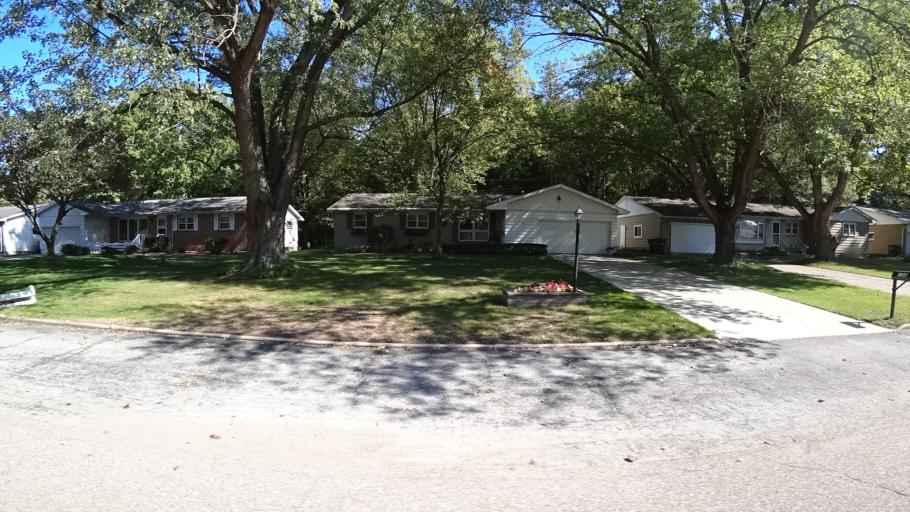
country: US
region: Indiana
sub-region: LaPorte County
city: Michigan City
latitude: 41.6926
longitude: -86.8829
